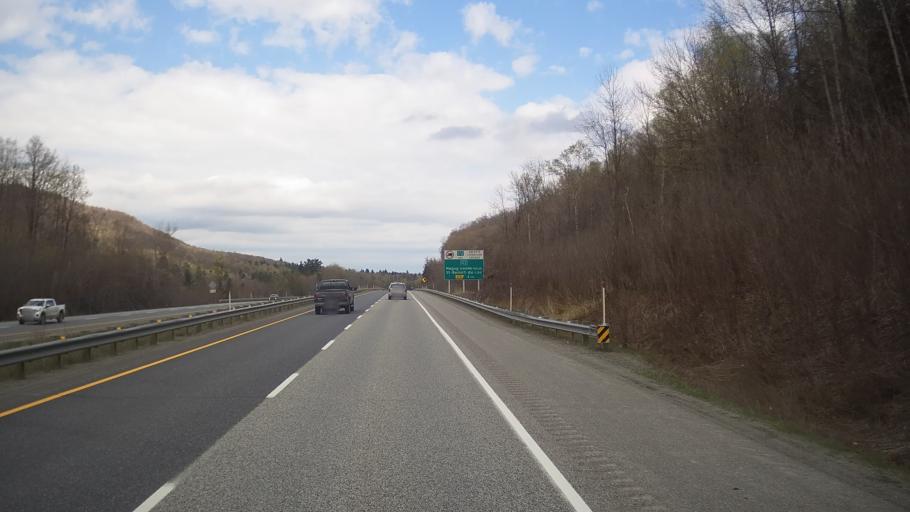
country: CA
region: Quebec
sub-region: Estrie
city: Magog
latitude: 45.2900
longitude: -72.2450
